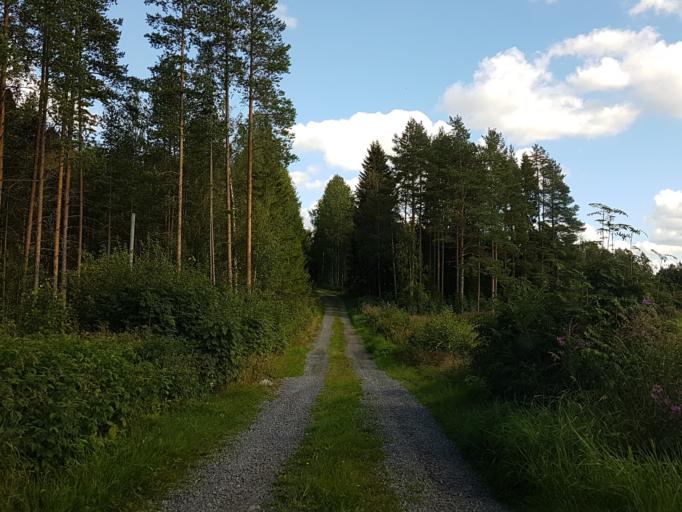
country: SE
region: Vaesterbotten
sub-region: Skelleftea Kommun
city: Burtraesk
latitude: 64.3629
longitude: 20.4817
